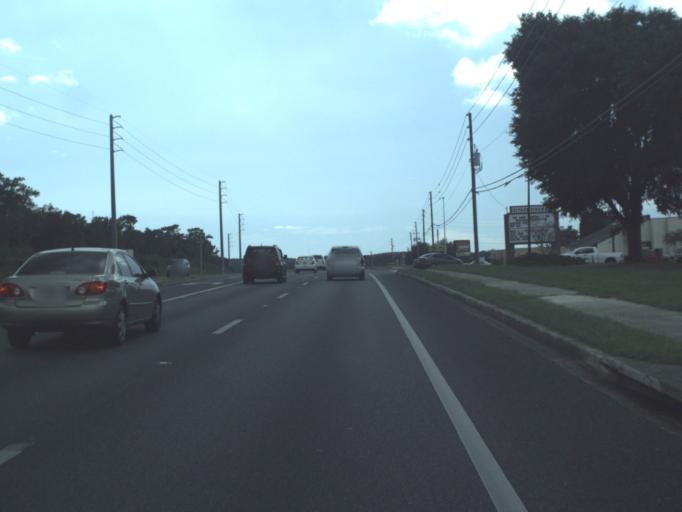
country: US
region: Florida
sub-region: Citrus County
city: Inverness Highlands North
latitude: 28.8540
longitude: -82.3888
